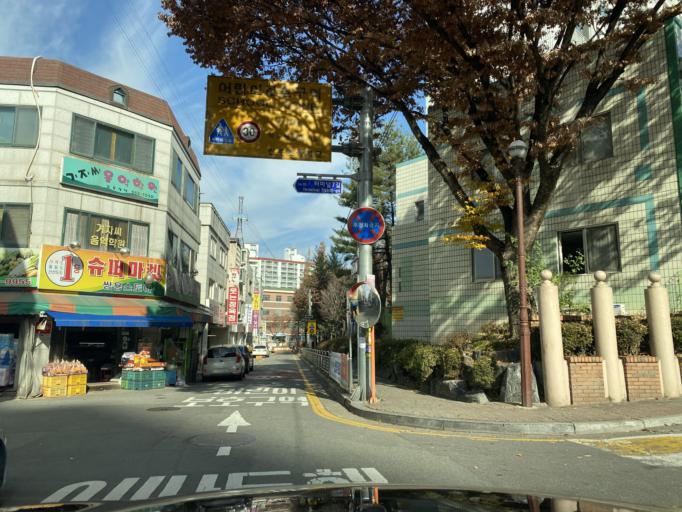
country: KR
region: Chungcheongnam-do
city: Cheonan
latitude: 36.8208
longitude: 127.1601
